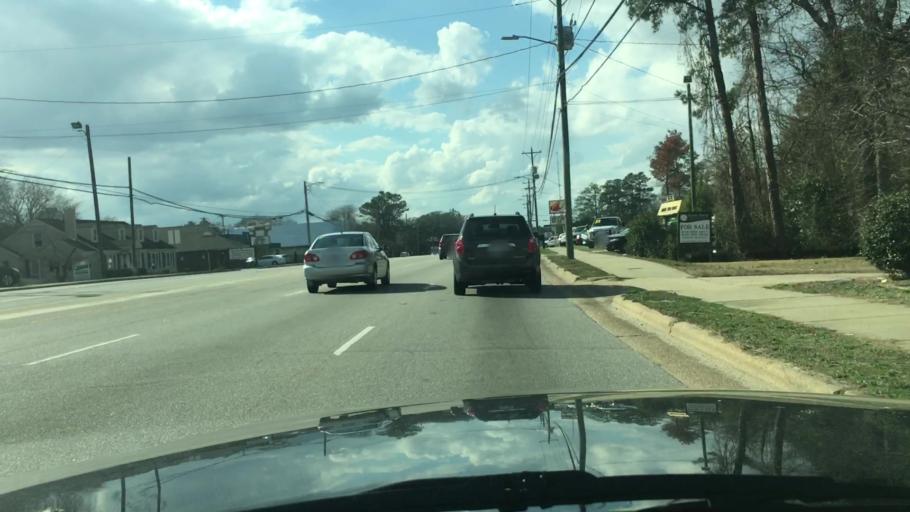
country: US
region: North Carolina
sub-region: Cumberland County
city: Hope Mills
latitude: 35.0426
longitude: -78.9678
